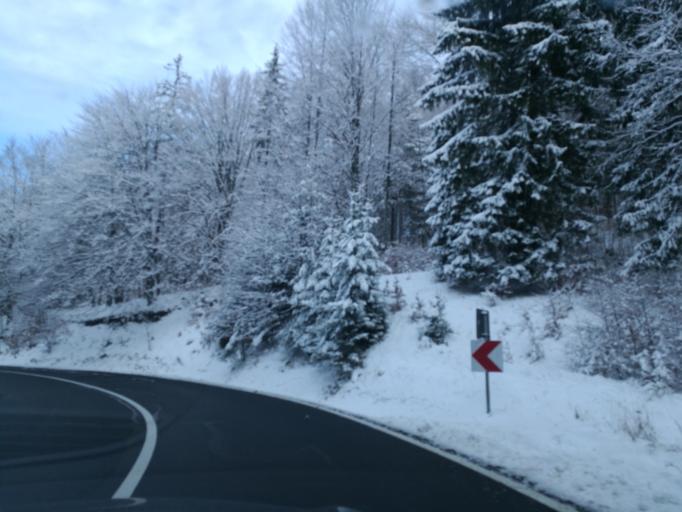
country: RO
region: Brasov
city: Brasov
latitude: 45.6033
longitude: 25.5551
